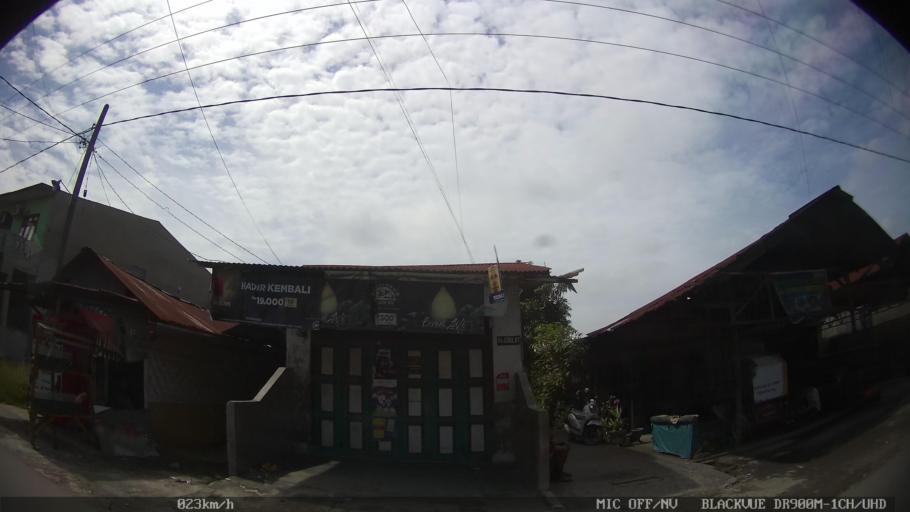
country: ID
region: North Sumatra
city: Medan
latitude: 3.5907
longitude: 98.7479
